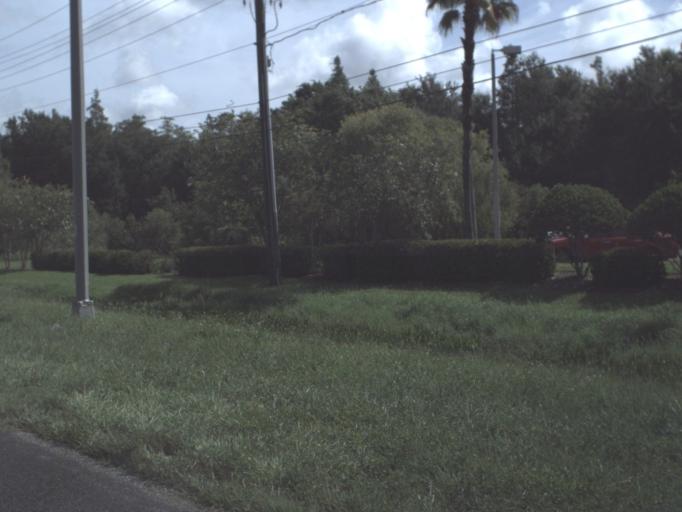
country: US
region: Florida
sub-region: Hillsborough County
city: Palm River-Clair Mel
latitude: 27.9451
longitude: -82.3536
